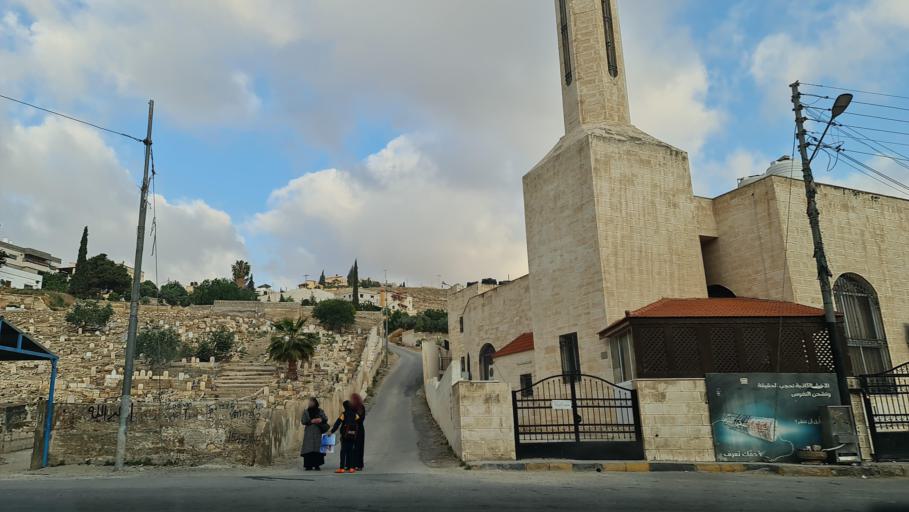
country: JO
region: Amman
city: Al Jubayhah
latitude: 32.0969
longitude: 35.9562
